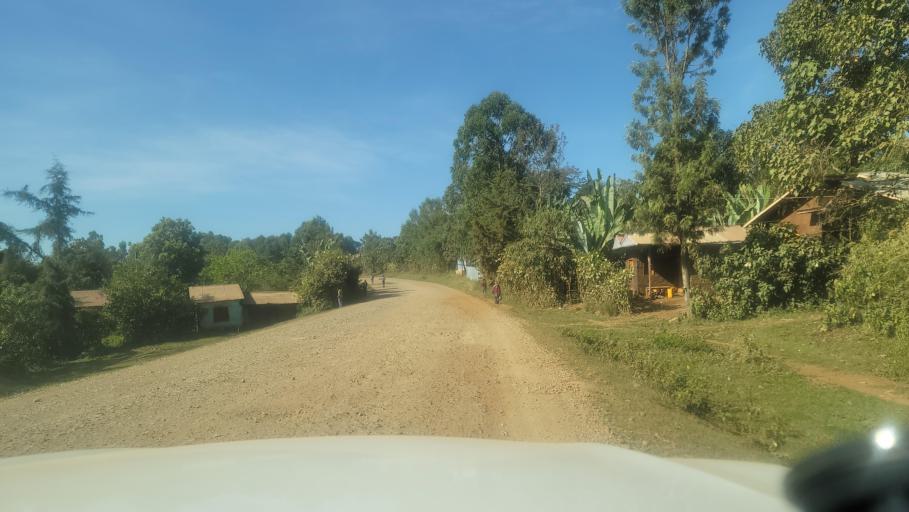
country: ET
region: Oromiya
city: Agaro
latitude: 7.7988
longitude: 36.4967
